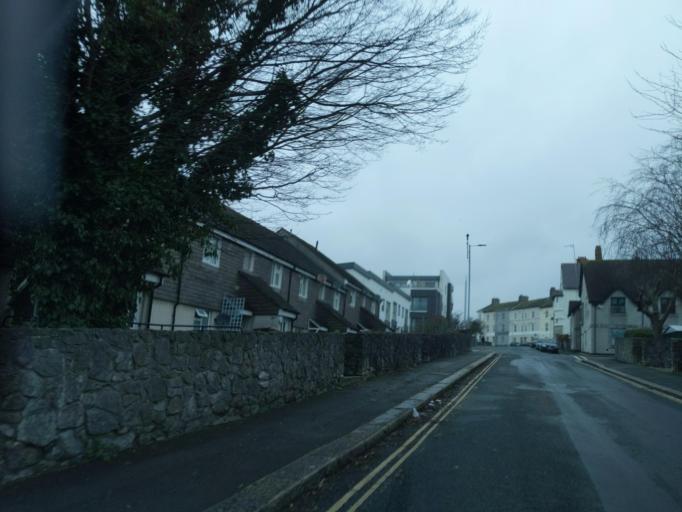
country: GB
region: England
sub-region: Plymouth
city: Plymouth
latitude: 50.3735
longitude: -4.1487
